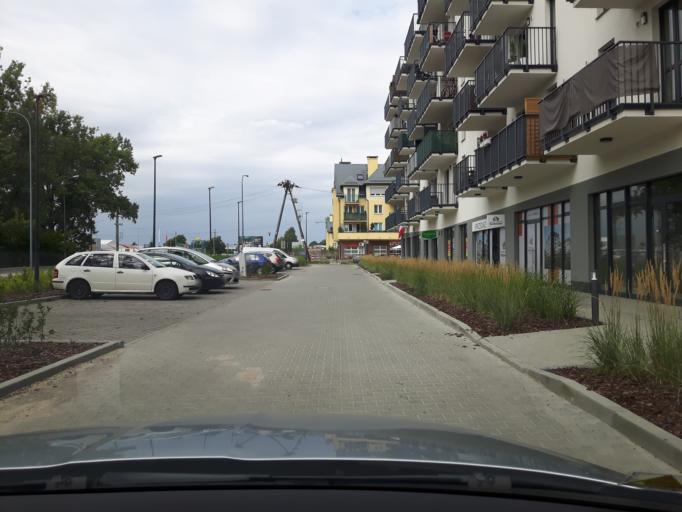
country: PL
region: Masovian Voivodeship
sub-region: Powiat wolominski
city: Zabki
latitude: 52.2748
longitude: 21.1175
